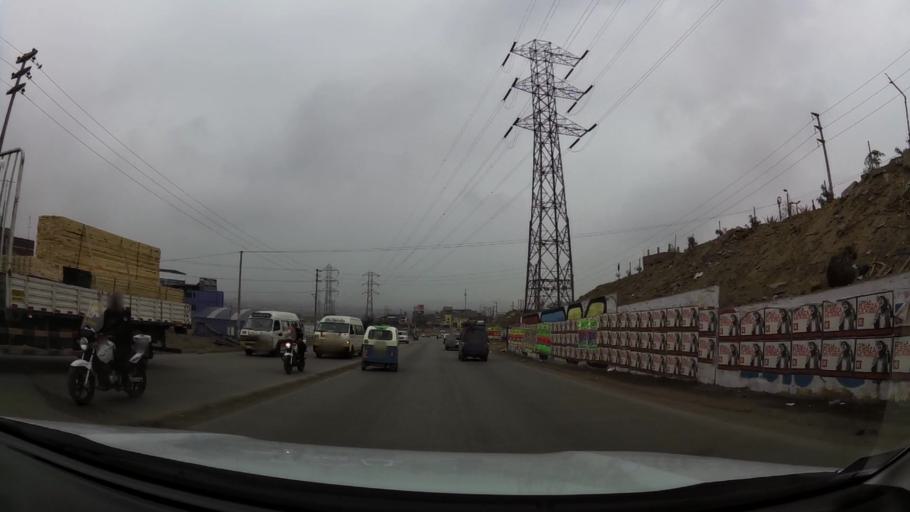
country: PE
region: Lima
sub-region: Lima
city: Surco
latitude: -12.2284
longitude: -76.9128
